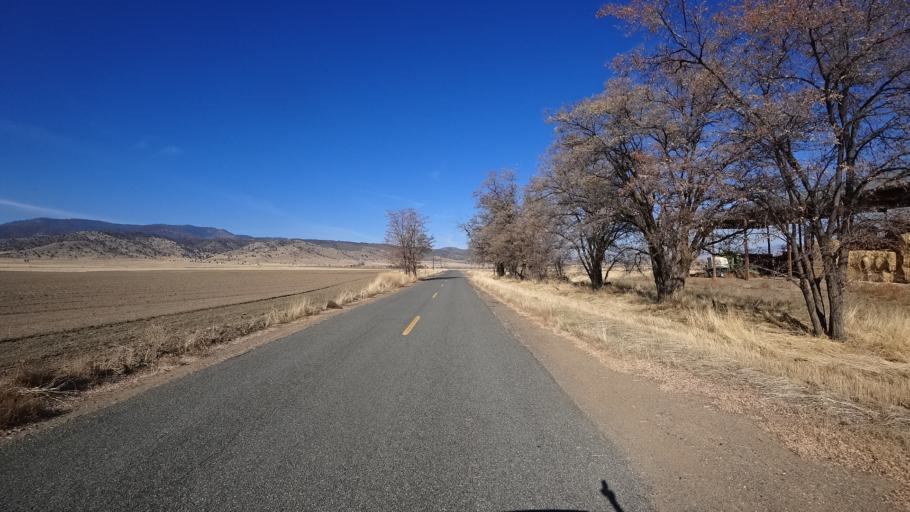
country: US
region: California
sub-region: Siskiyou County
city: Montague
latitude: 41.5588
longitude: -122.5468
